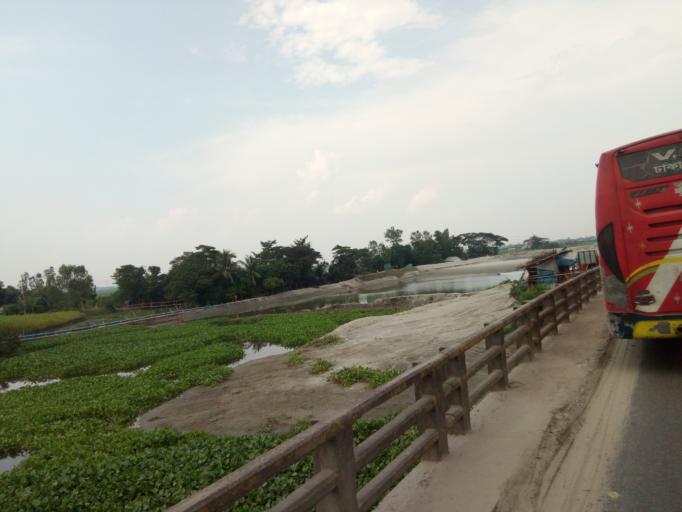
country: BD
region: Dhaka
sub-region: Dhaka
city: Dhaka
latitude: 23.6160
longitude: 90.3327
